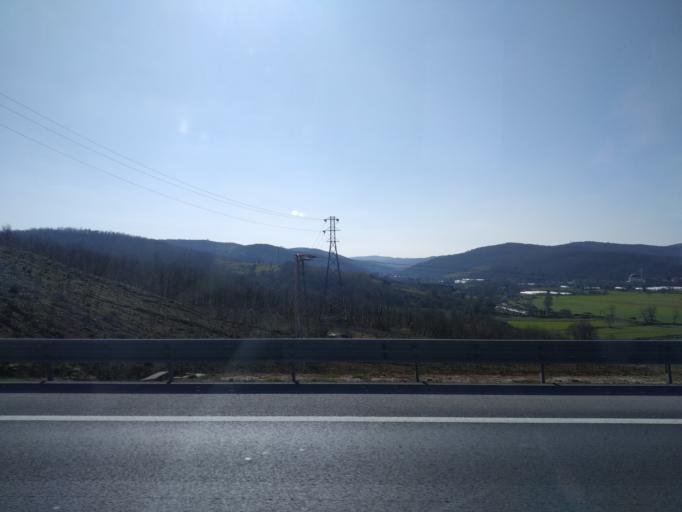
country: TR
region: Istanbul
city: Mahmut Sevket Pasa
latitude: 41.1865
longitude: 29.2157
